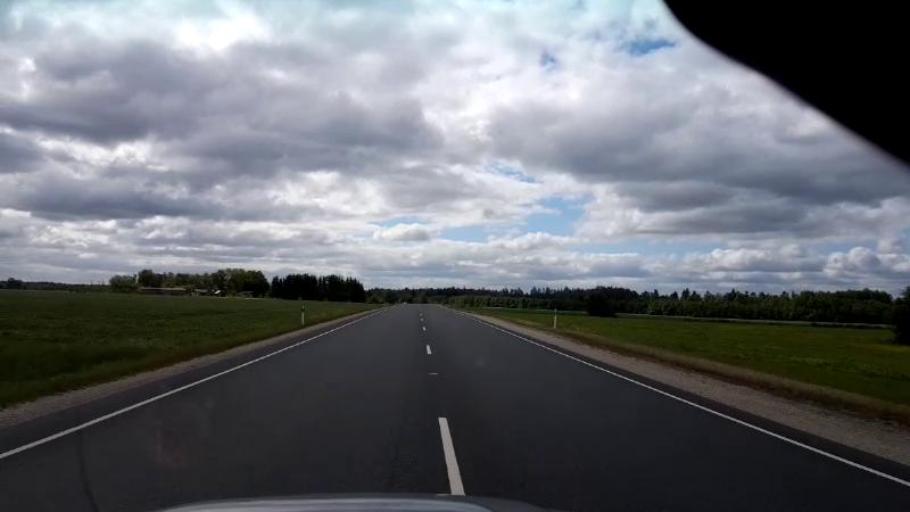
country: EE
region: Paernumaa
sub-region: Halinga vald
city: Parnu-Jaagupi
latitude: 58.6899
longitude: 24.4353
